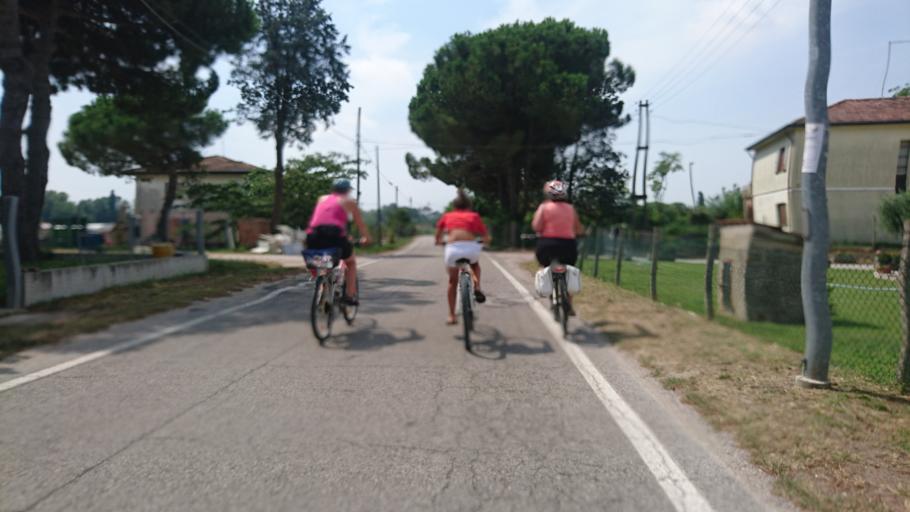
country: IT
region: Veneto
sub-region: Provincia di Rovigo
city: Rosolina
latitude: 45.0830
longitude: 12.2330
